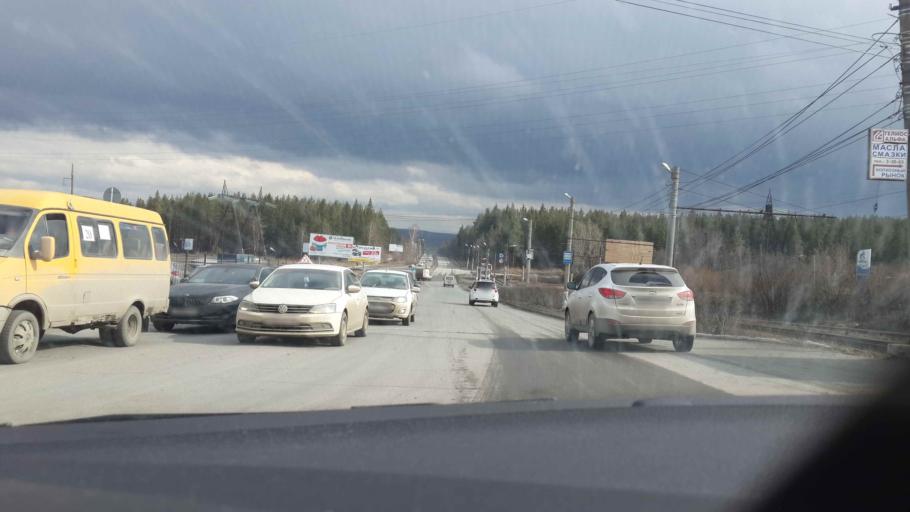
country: RU
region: Chelyabinsk
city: Zlatoust
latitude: 55.1379
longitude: 59.6697
